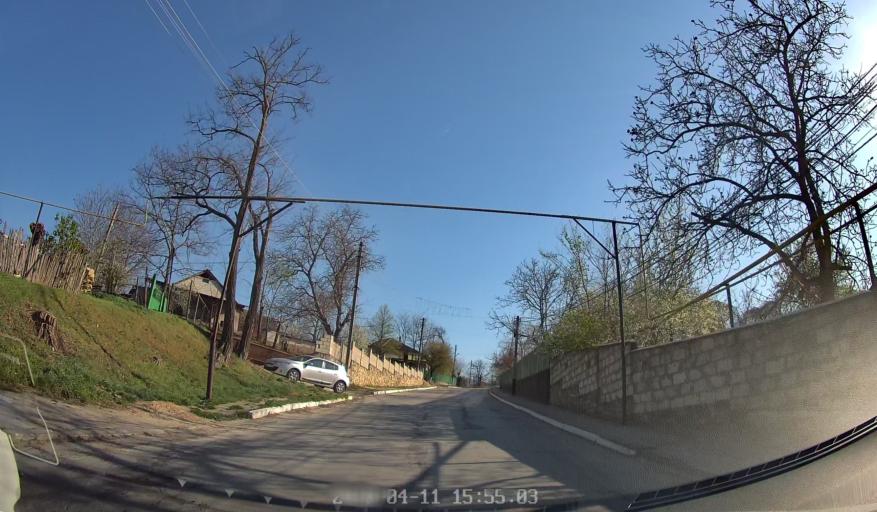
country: MD
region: Chisinau
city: Vadul lui Voda
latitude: 47.0975
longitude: 29.1773
